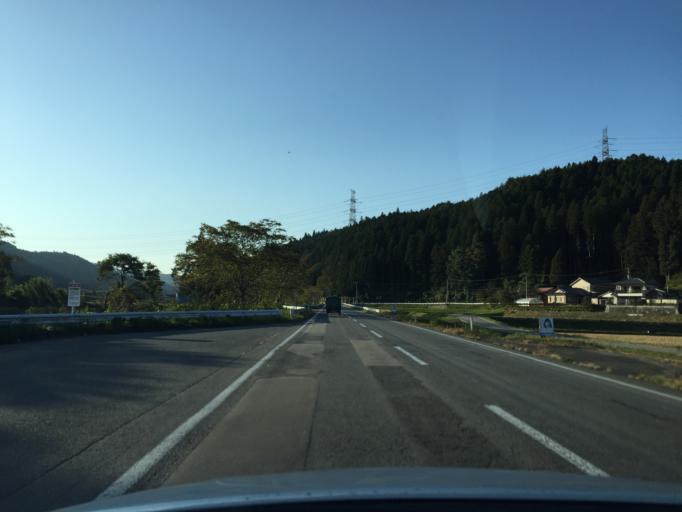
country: JP
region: Fukushima
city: Iwaki
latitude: 37.1348
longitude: 140.7095
